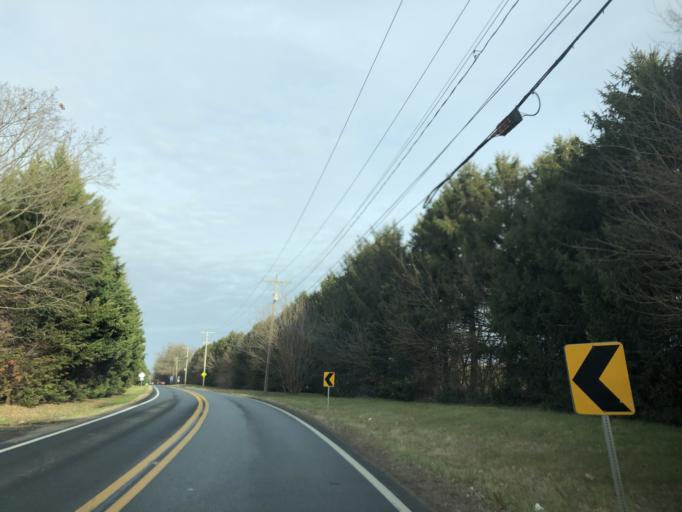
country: US
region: Delaware
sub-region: New Castle County
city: Townsend
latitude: 39.4407
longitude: -75.6437
